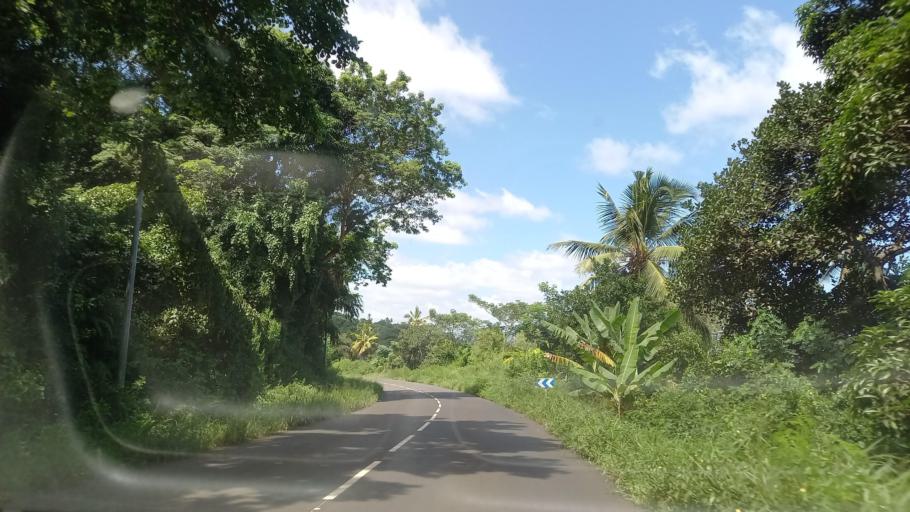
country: YT
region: Acoua
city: Acoua
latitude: -12.7488
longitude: 45.0599
